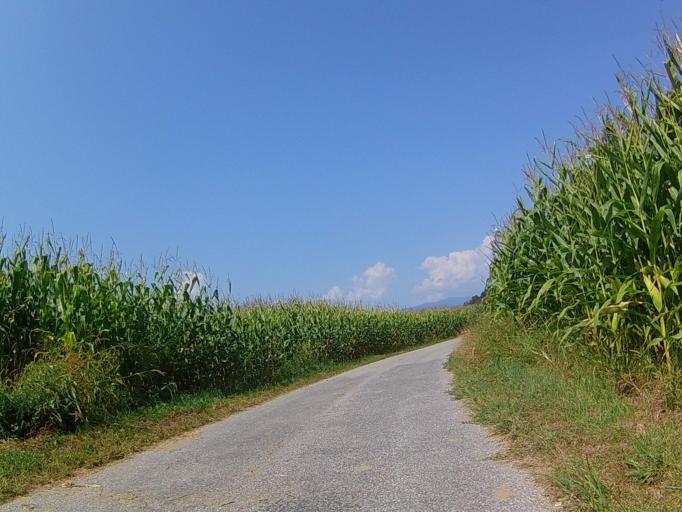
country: AT
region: Styria
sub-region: Politischer Bezirk Leibnitz
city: Oberhaag
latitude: 46.6960
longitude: 15.3198
